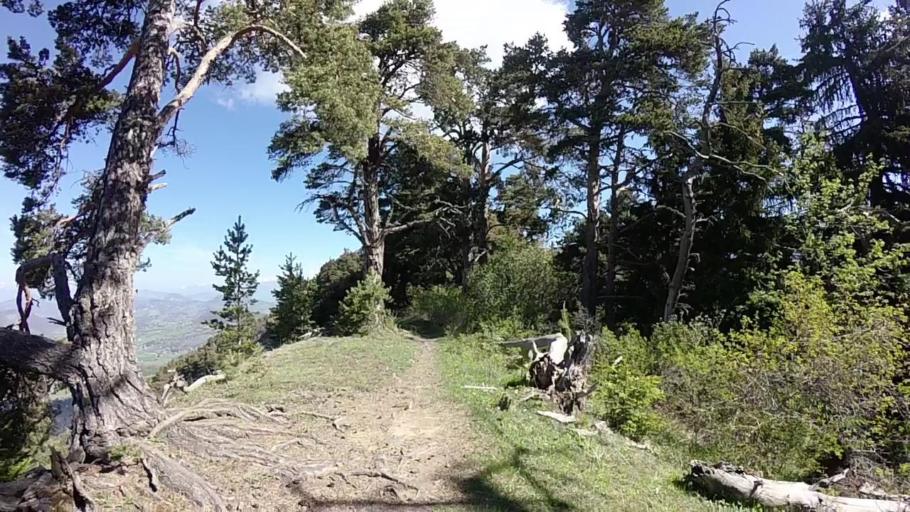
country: FR
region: Provence-Alpes-Cote d'Azur
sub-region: Departement des Alpes-de-Haute-Provence
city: Seyne-les-Alpes
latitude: 44.3203
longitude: 6.3737
